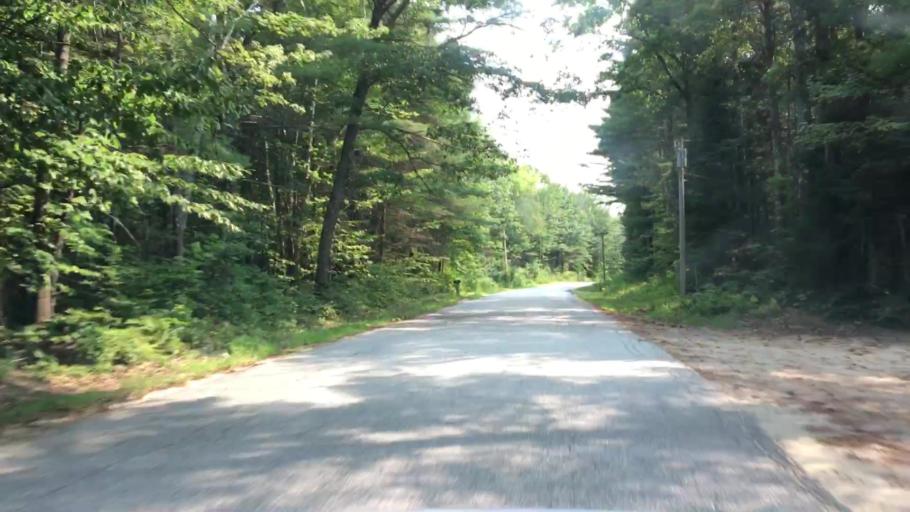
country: US
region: Maine
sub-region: Androscoggin County
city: Livermore
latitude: 44.3329
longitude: -70.2906
